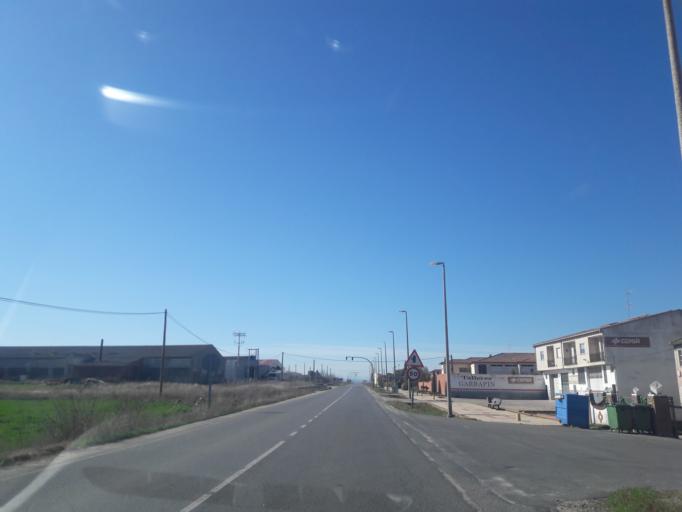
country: ES
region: Castille and Leon
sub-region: Provincia de Salamanca
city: Macotera
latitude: 40.8296
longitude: -5.2796
